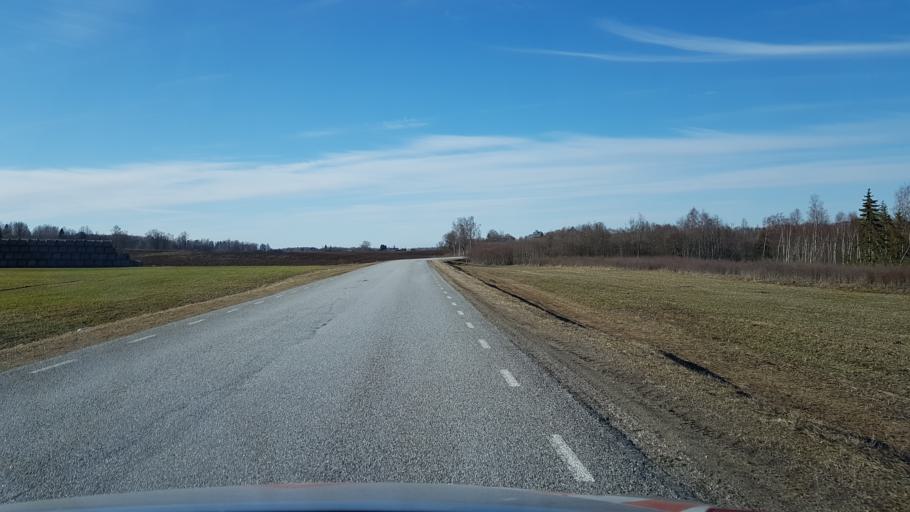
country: EE
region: Laeaene-Virumaa
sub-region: Kadrina vald
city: Kadrina
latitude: 59.3011
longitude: 26.1616
